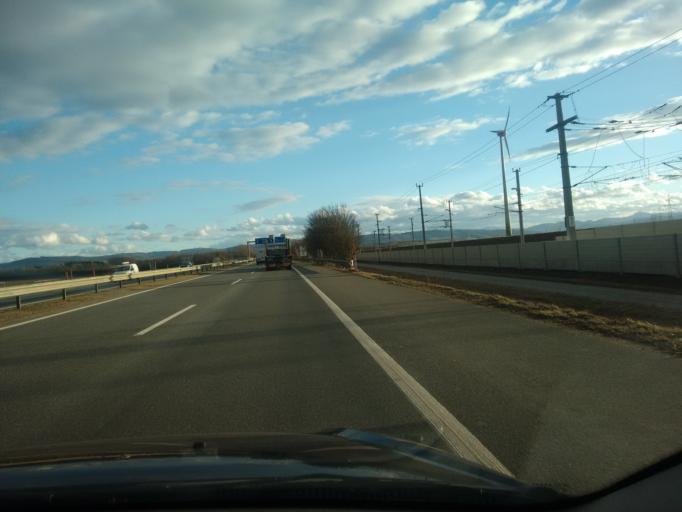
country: AT
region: Lower Austria
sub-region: Sankt Polten Stadt
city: Sankt Poelten
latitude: 48.1888
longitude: 15.6604
